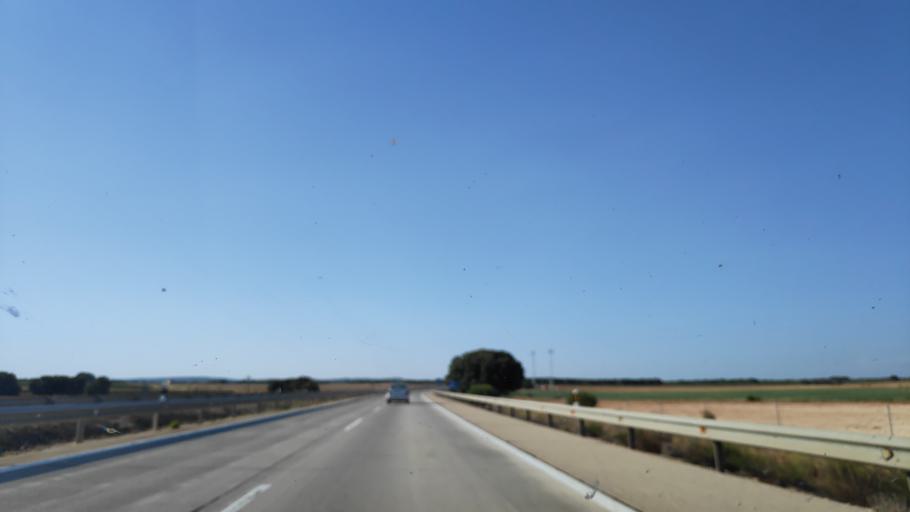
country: ES
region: Castille-La Mancha
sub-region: Provincia de Cuenca
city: Pozoamargo
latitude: 39.3162
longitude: -2.2035
